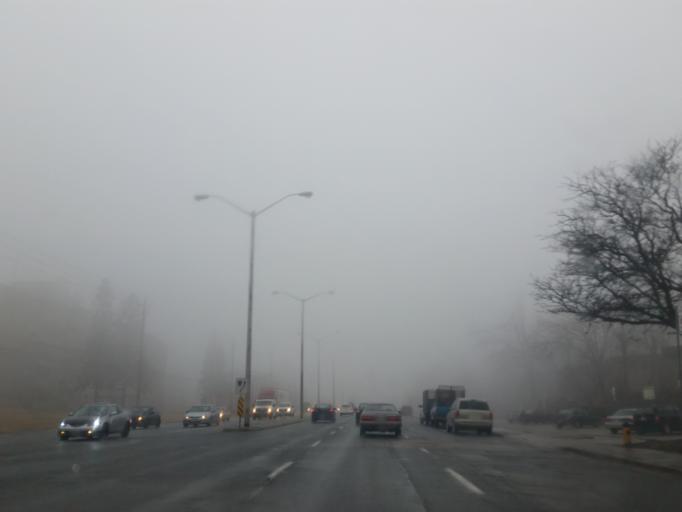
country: CA
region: Ontario
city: Scarborough
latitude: 43.7305
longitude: -79.2265
